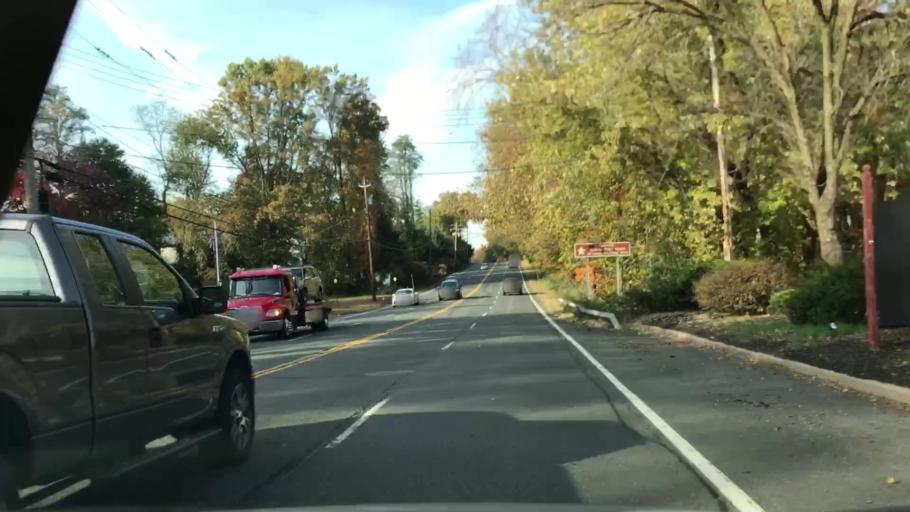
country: US
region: New York
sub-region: Rockland County
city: Tappan
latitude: 41.0250
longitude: -73.9430
